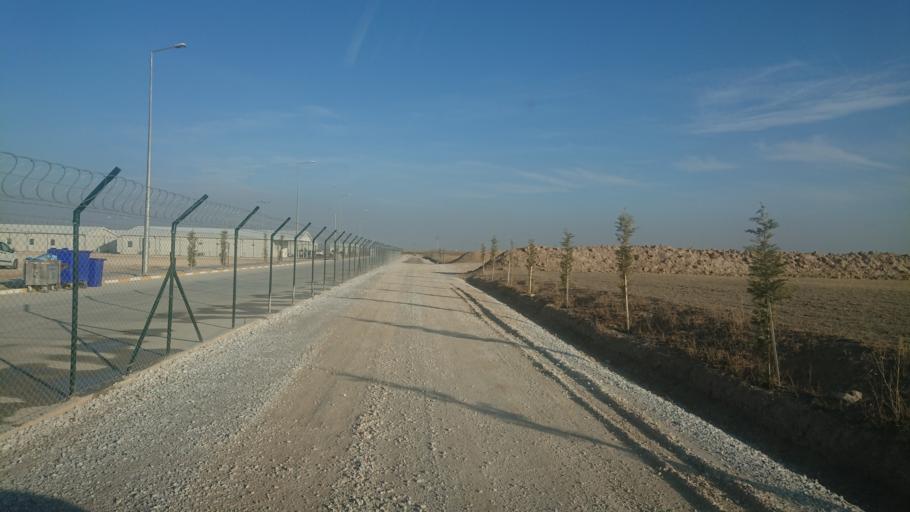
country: TR
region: Aksaray
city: Sultanhani
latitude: 38.1467
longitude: 33.5906
